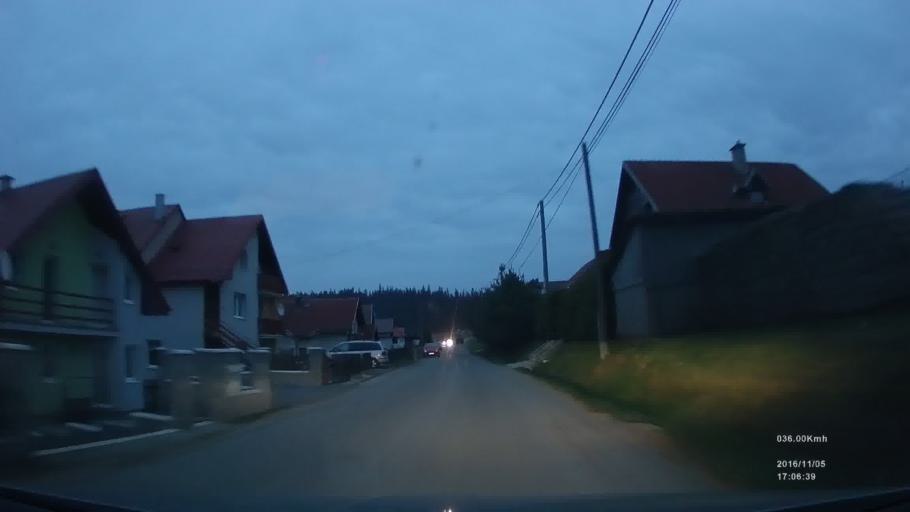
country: SK
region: Presovsky
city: Lubica
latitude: 49.0489
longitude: 20.5024
